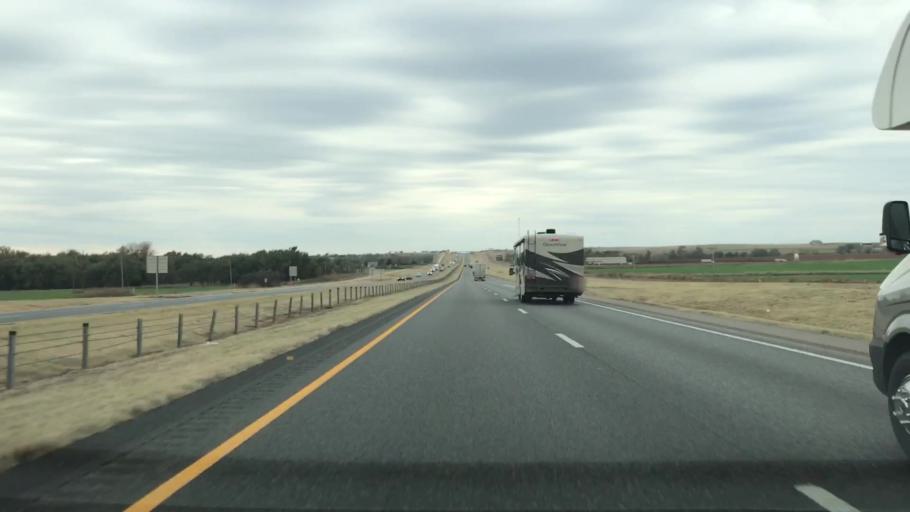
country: US
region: Oklahoma
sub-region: Custer County
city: Clinton
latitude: 35.5161
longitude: -98.8729
